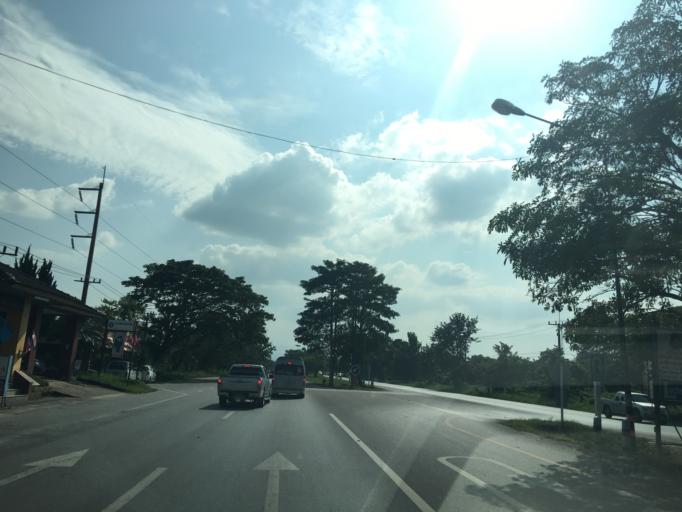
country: TH
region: Chiang Rai
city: Mae Lao
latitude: 19.7344
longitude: 99.7203
